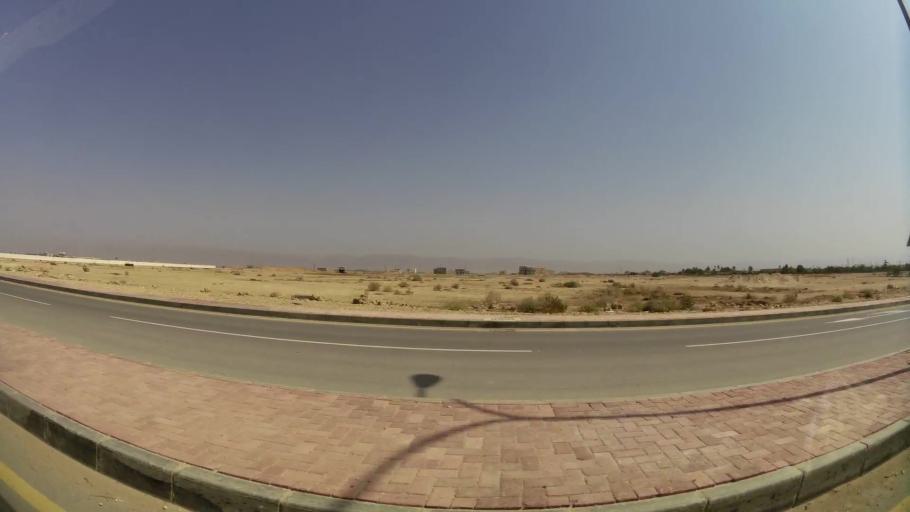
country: OM
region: Zufar
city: Salalah
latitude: 17.0319
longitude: 54.1370
